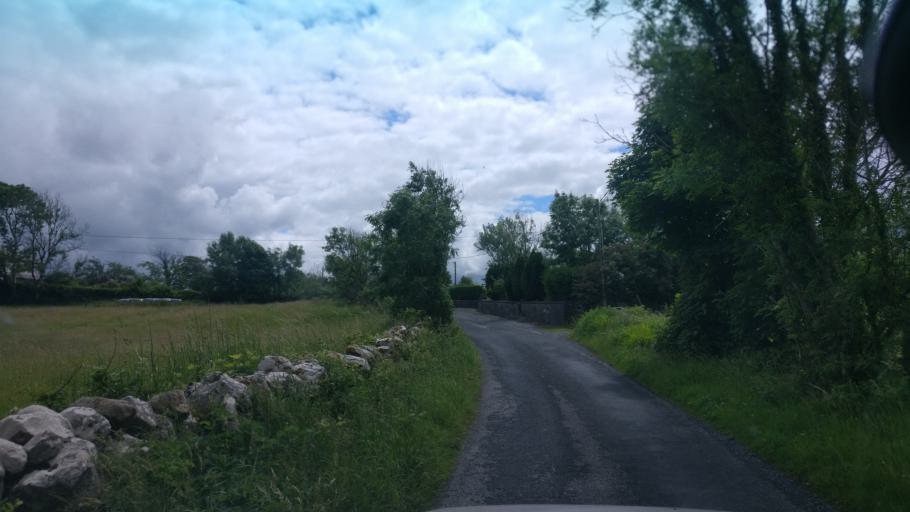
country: IE
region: Connaught
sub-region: County Galway
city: Loughrea
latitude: 53.1519
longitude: -8.5672
